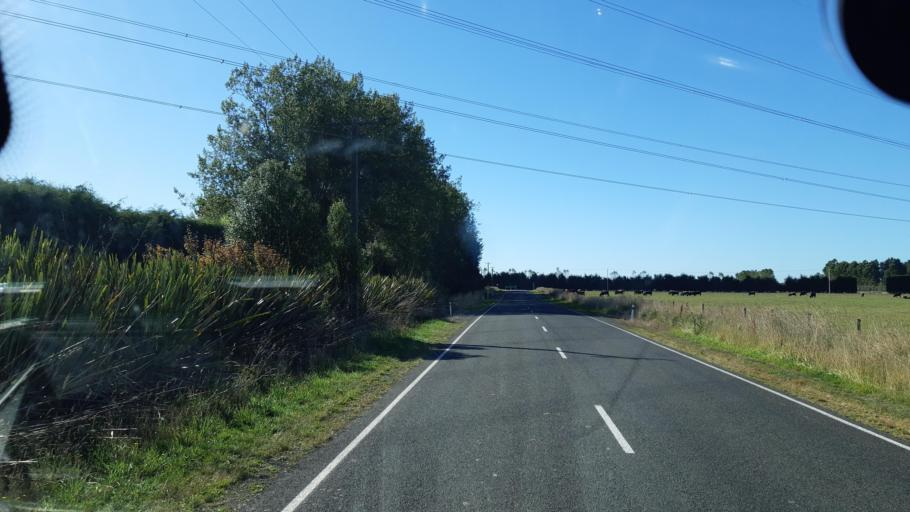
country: NZ
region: Southland
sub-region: Southland District
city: Winton
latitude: -46.1583
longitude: 168.1464
